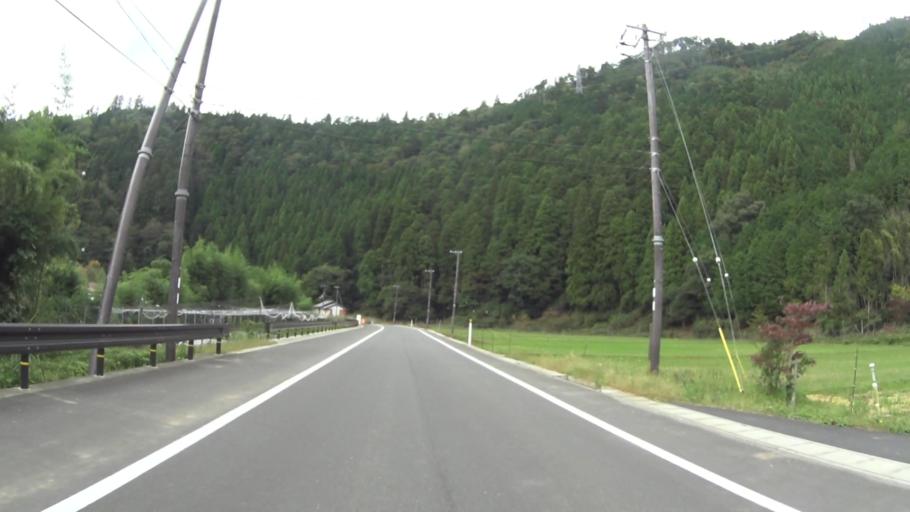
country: JP
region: Fukui
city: Obama
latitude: 35.3202
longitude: 135.6531
